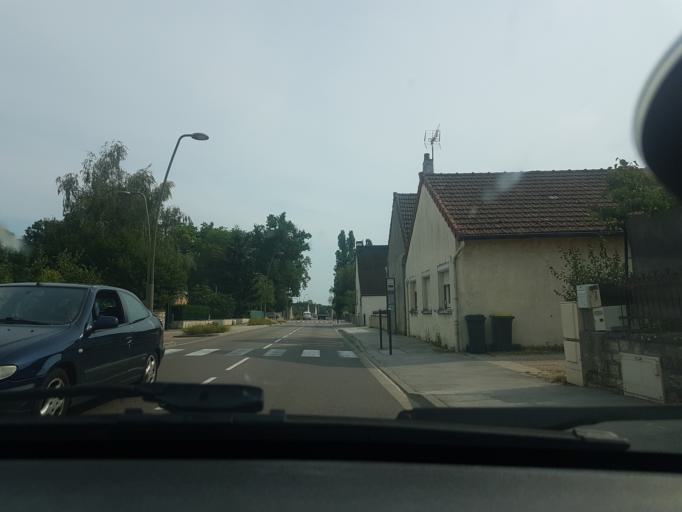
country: FR
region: Bourgogne
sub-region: Departement de Saone-et-Loire
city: Saint-Marcel
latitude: 46.7685
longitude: 4.8935
